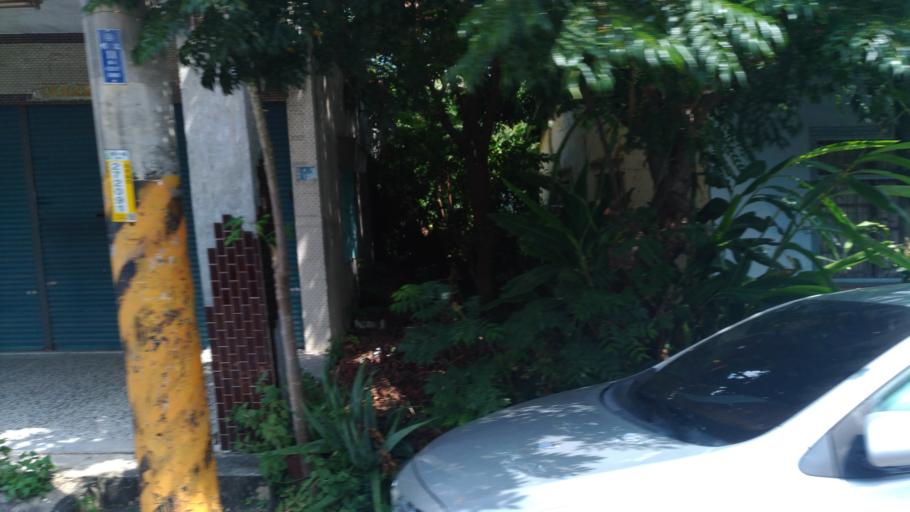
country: TW
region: Taiwan
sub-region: Yunlin
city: Douliu
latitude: 23.7593
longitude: 120.5028
